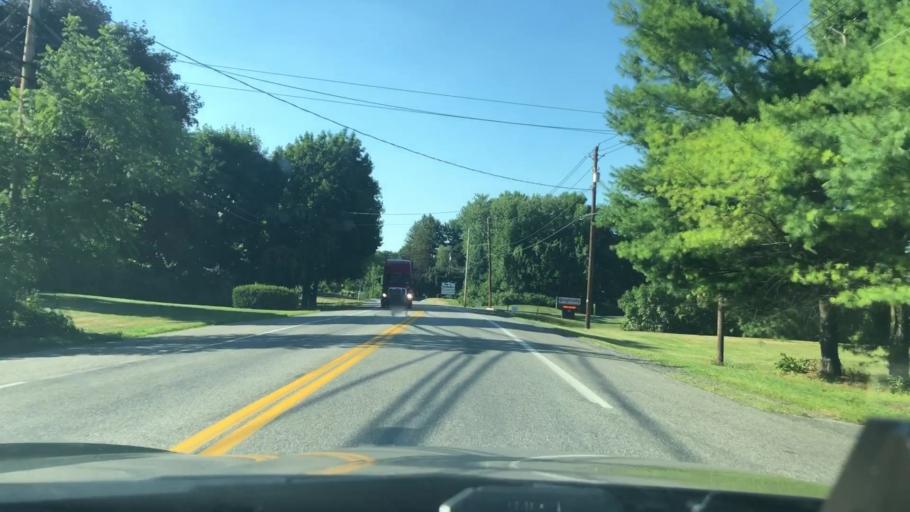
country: US
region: Pennsylvania
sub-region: Cumberland County
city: Mechanicsburg
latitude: 40.2337
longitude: -77.0065
